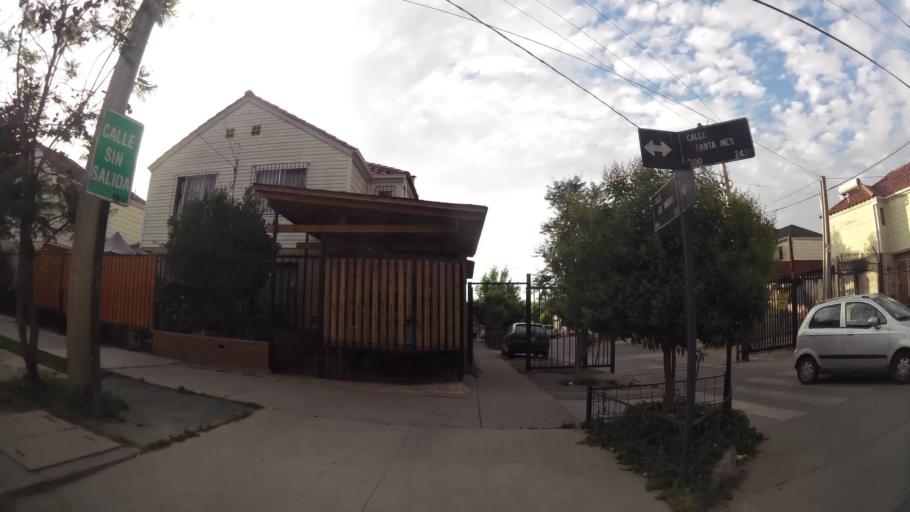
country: CL
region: Santiago Metropolitan
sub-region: Provincia de Maipo
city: San Bernardo
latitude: -33.6234
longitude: -70.6866
